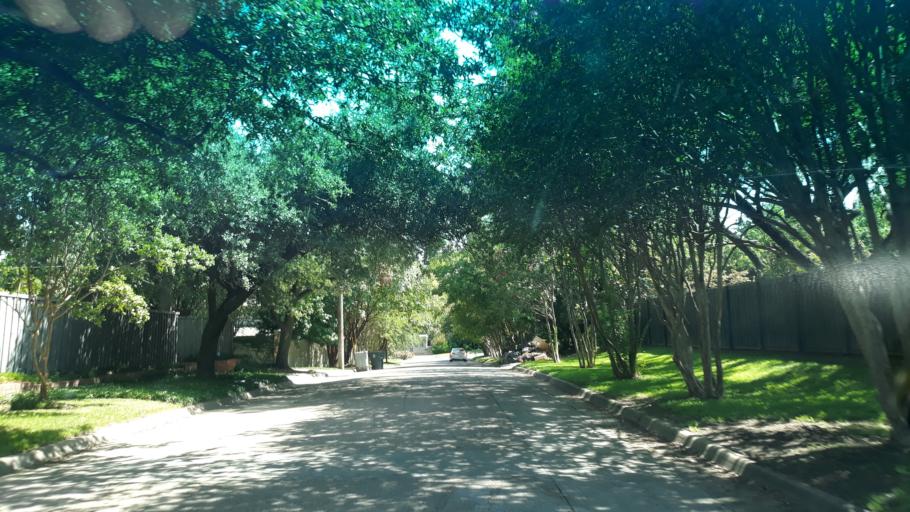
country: US
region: Texas
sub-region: Dallas County
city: Highland Park
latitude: 32.8207
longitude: -96.7427
